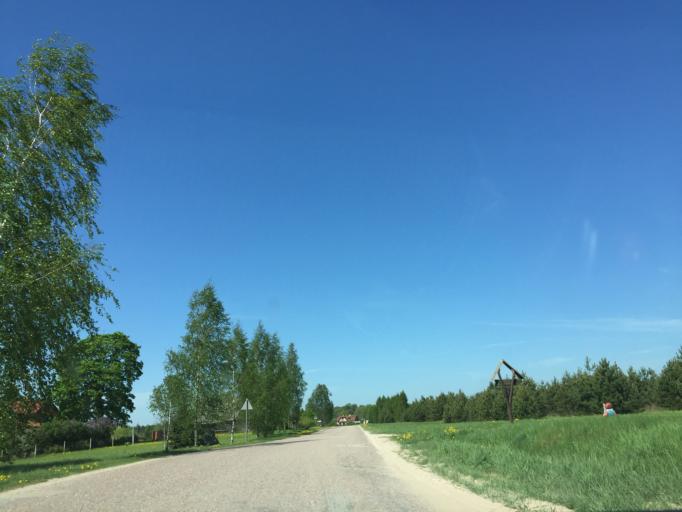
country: LV
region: Ogre
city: Ogre
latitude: 56.8529
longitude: 24.7089
